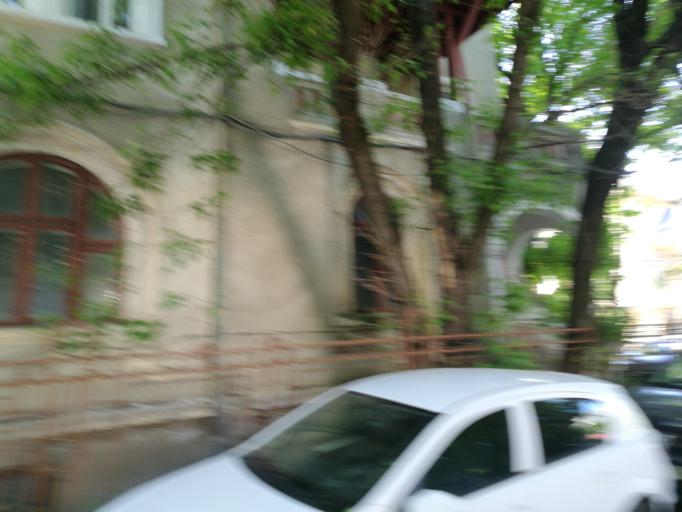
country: RO
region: Bucuresti
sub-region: Municipiul Bucuresti
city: Bucuresti
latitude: 44.4339
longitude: 26.0702
